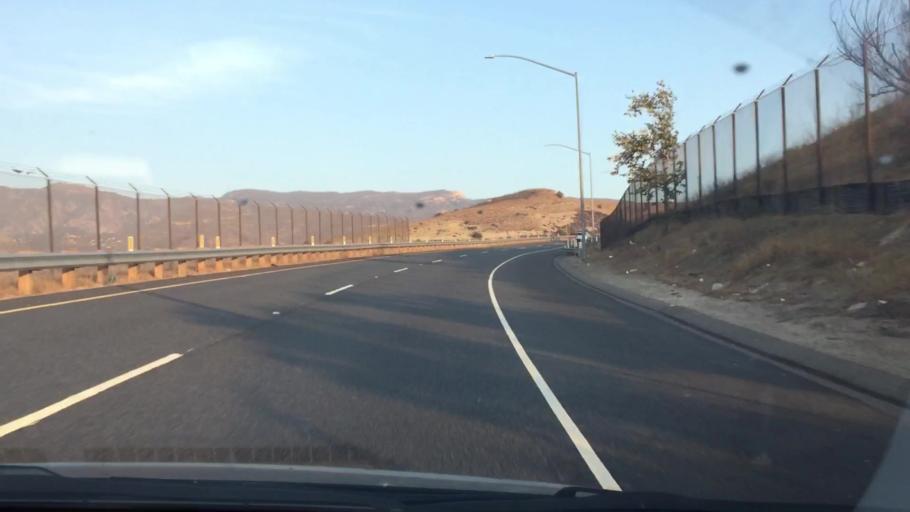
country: US
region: California
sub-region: Orange County
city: Yorba Linda
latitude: 33.8651
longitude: -117.7197
